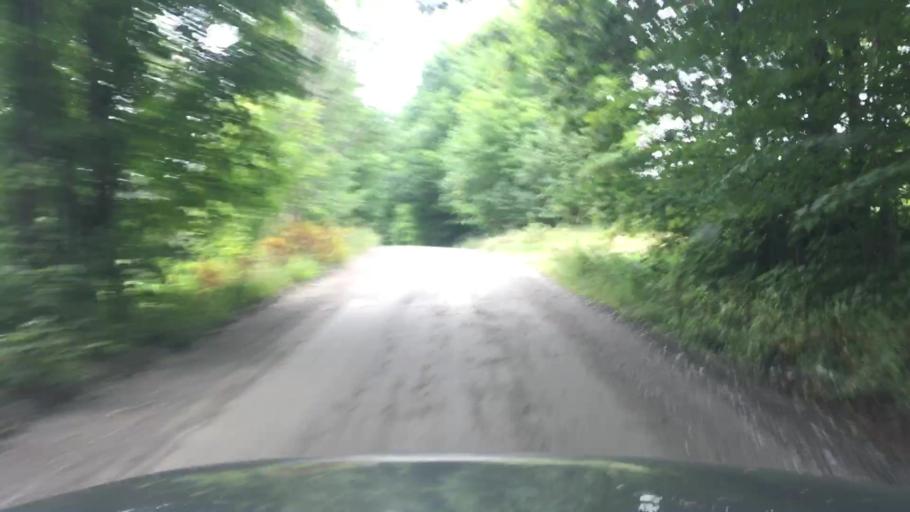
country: US
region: Vermont
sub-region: Windham County
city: Dover
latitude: 42.8625
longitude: -72.7809
